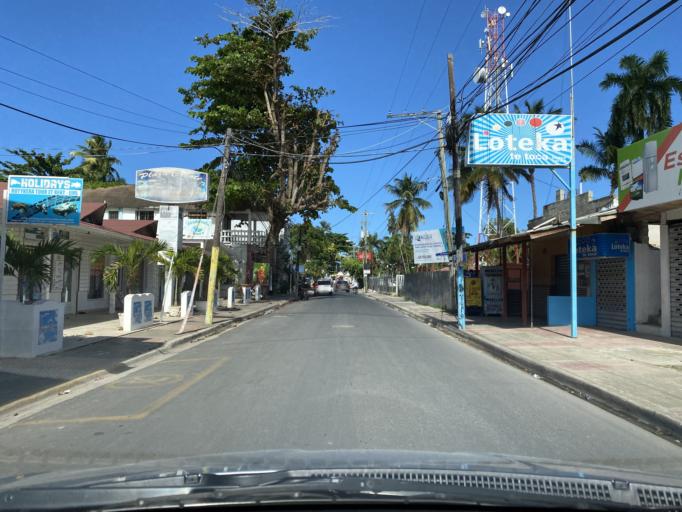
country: DO
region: Samana
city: Las Terrenas
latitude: 19.3198
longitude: -69.5389
